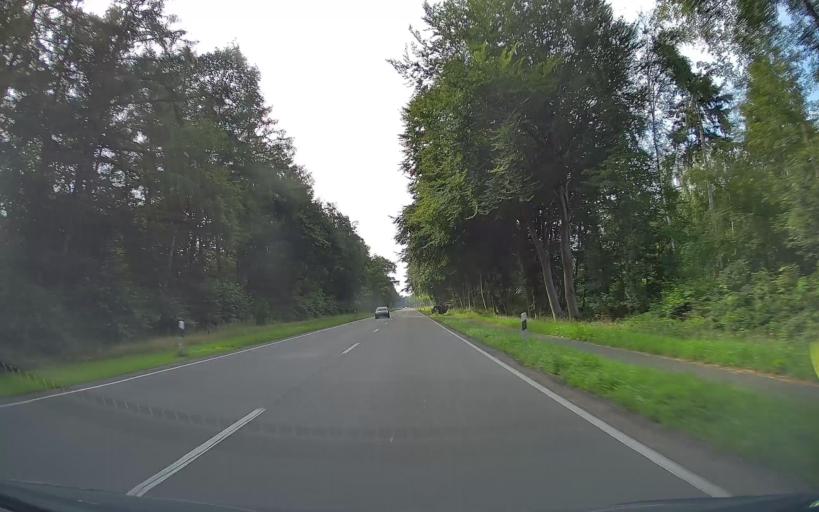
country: DE
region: Lower Saxony
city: Friesoythe
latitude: 52.9911
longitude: 7.8849
